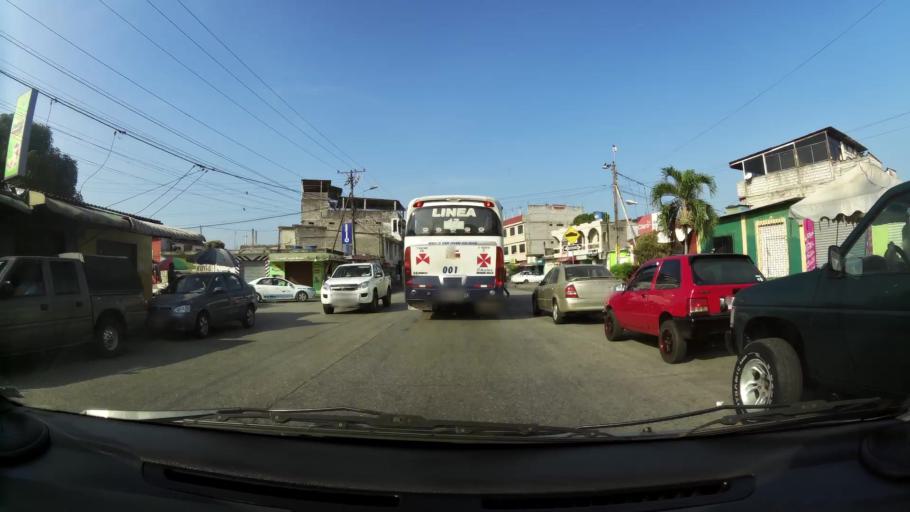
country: EC
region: Guayas
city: Eloy Alfaro
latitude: -2.1776
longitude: -79.8440
